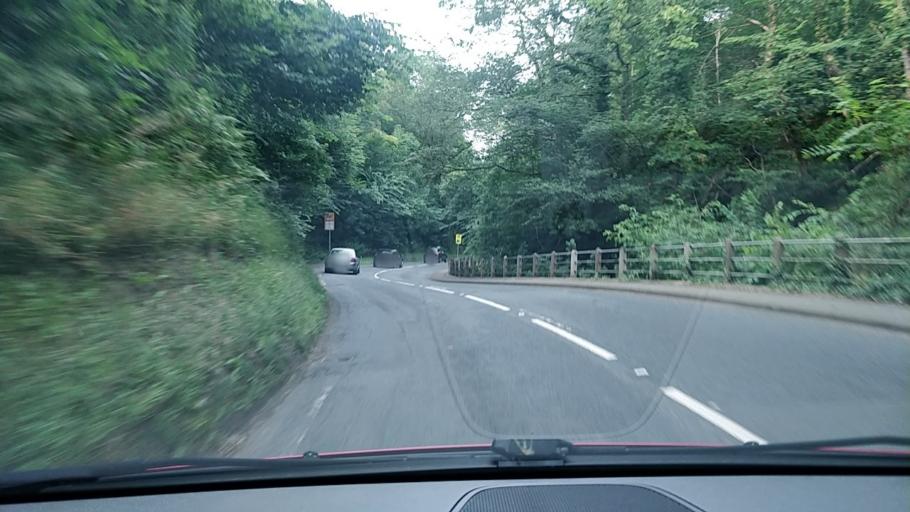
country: GB
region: Wales
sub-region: County of Flintshire
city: Leeswood
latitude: 53.1291
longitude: -3.0851
